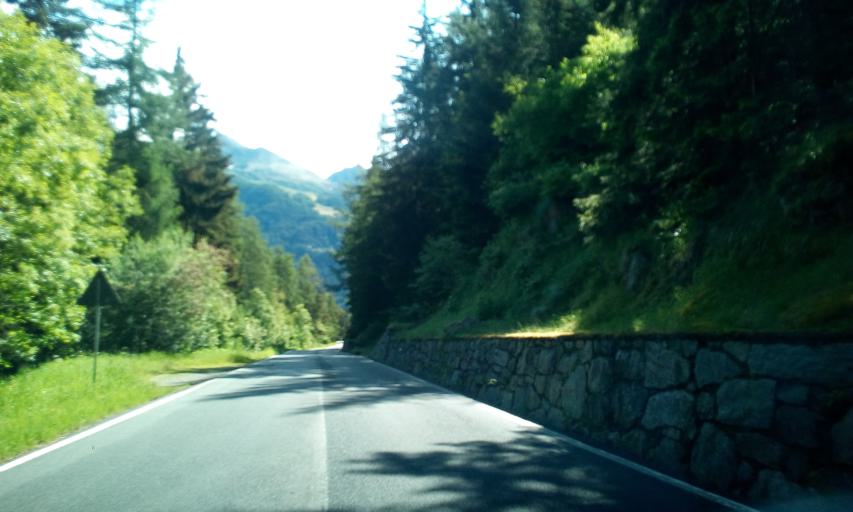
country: IT
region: Aosta Valley
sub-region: Valle d'Aosta
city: Brusson
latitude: 45.7544
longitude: 7.7167
